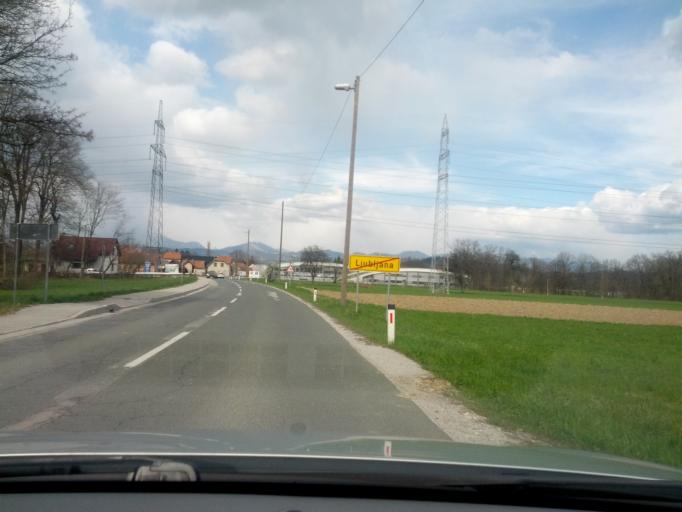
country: SI
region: Dol pri Ljubljani
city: Dol pri Ljubljani
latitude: 46.1018
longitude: 14.5907
